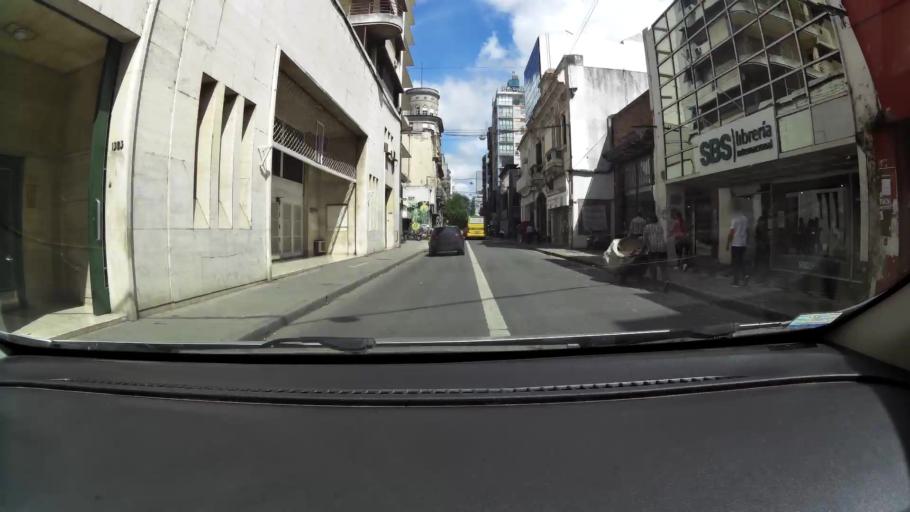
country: AR
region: Santa Fe
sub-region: Departamento de Rosario
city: Rosario
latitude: -32.9445
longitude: -60.6410
